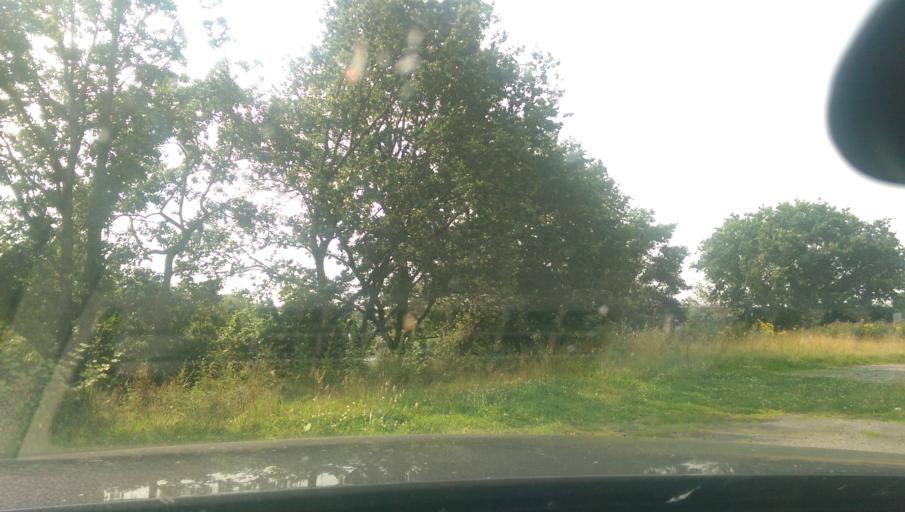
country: NL
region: North Brabant
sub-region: Gemeente Eersel
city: Eersel
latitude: 51.3775
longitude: 5.3148
